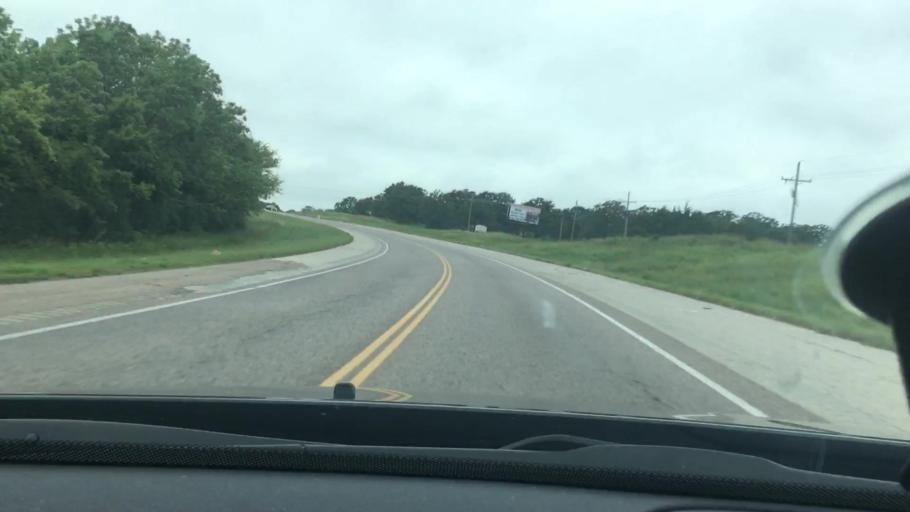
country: US
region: Oklahoma
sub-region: Pontotoc County
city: Ada
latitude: 34.7868
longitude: -96.5715
